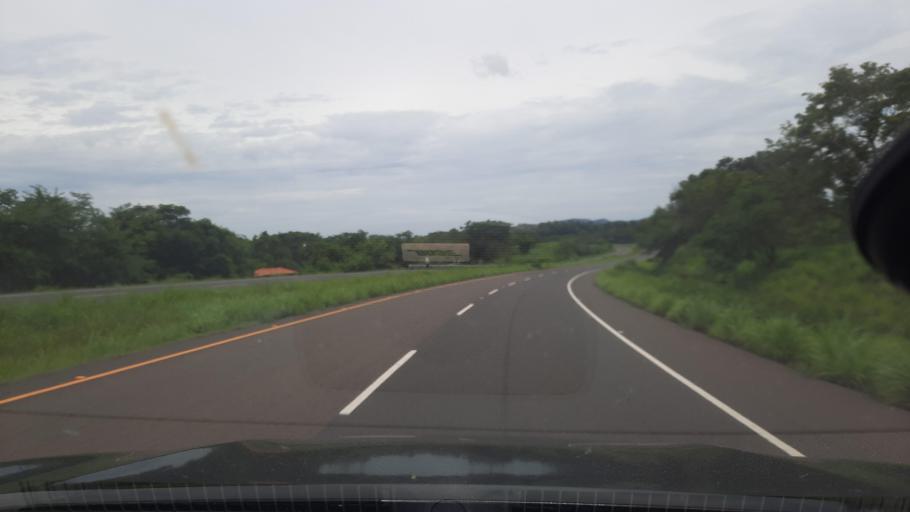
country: HN
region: Valle
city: Aramecina
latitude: 13.7707
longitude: -87.7020
